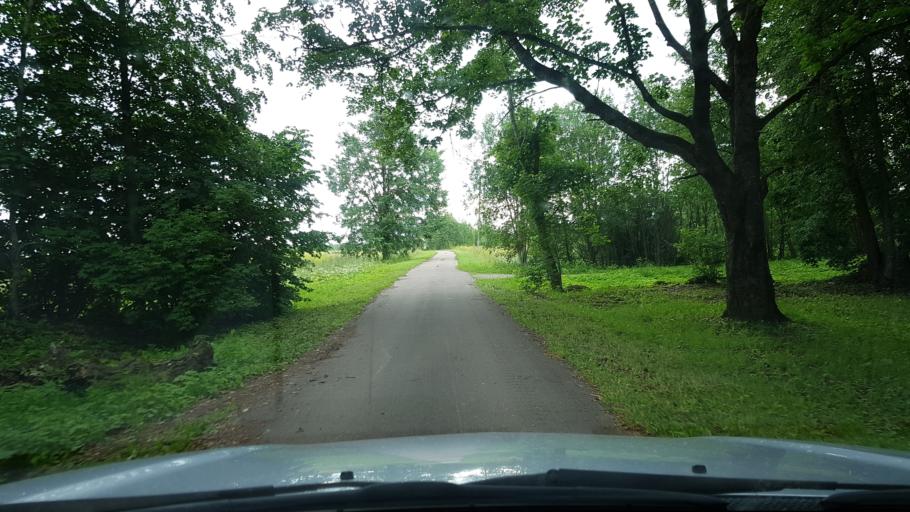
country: EE
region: Ida-Virumaa
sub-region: Narva-Joesuu linn
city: Narva-Joesuu
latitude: 59.3881
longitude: 27.9820
